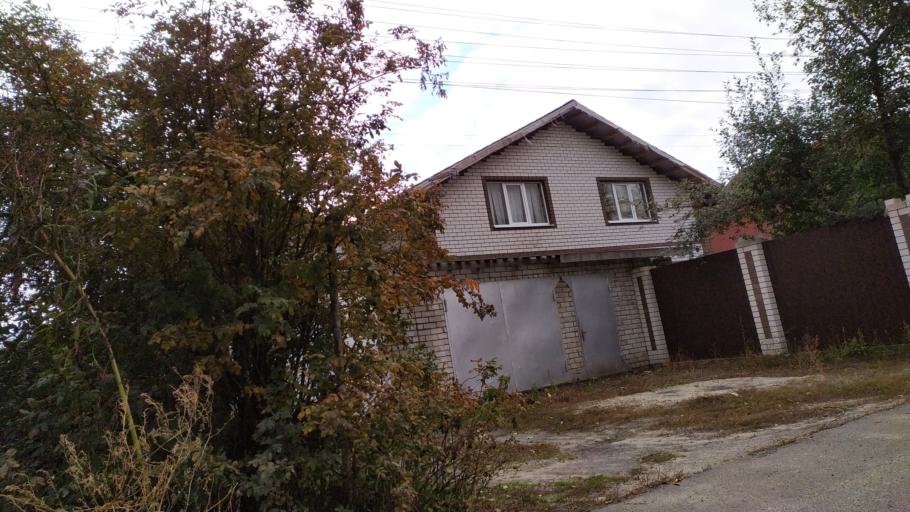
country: RU
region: Kursk
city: Kursk
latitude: 51.6473
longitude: 36.1490
